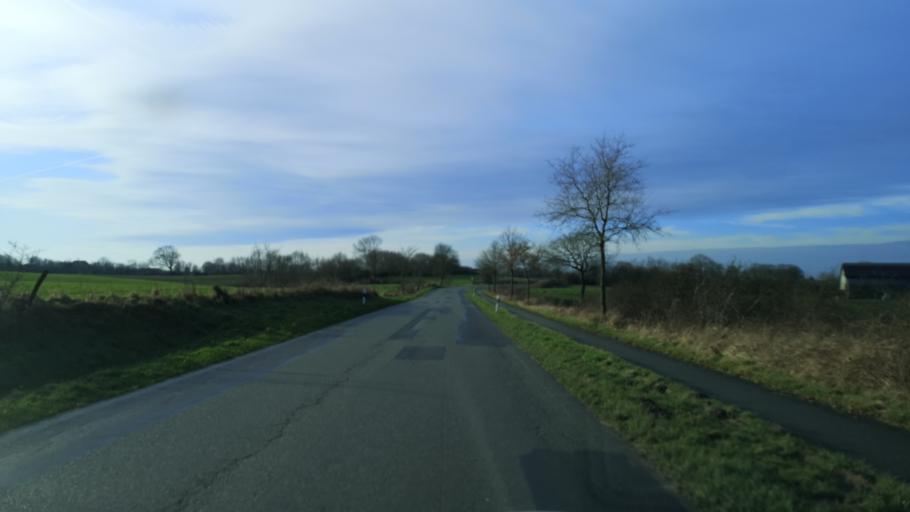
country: DE
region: Schleswig-Holstein
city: Havetoft
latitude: 54.6575
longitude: 9.5265
